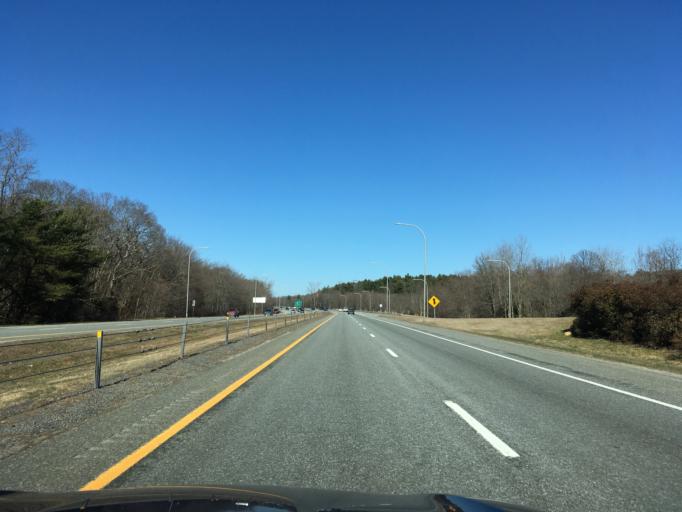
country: US
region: Rhode Island
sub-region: Kent County
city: East Greenwich
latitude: 41.6150
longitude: -71.4905
